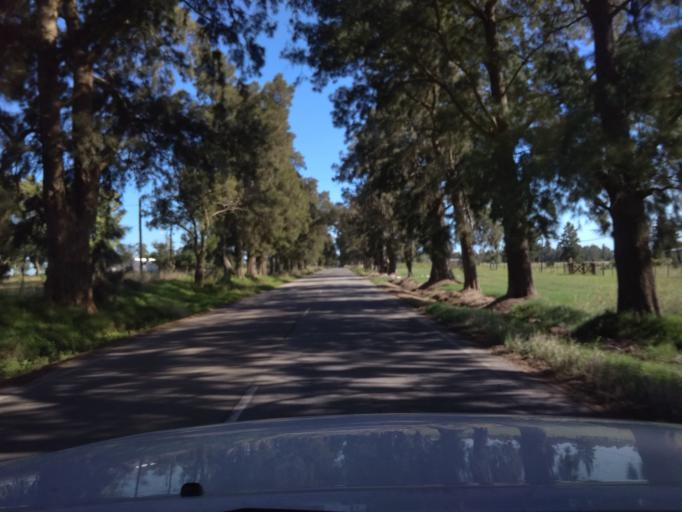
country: UY
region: Canelones
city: San Bautista
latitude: -34.3871
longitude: -55.9595
